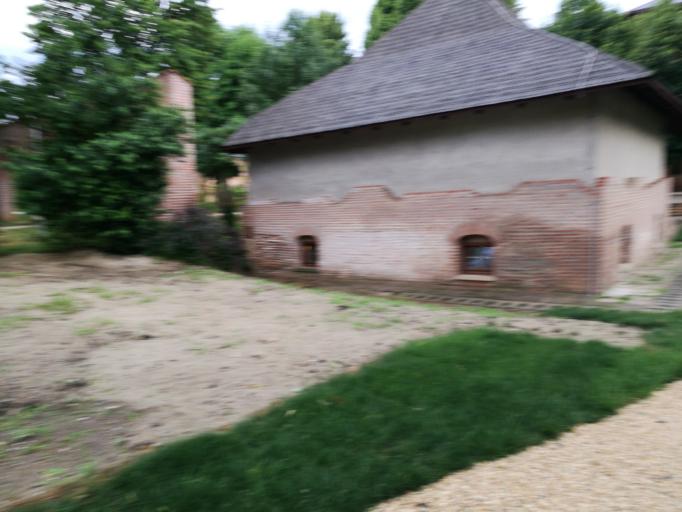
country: RO
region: Ilfov
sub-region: Comuna Mogosoaia
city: Mogosoaia
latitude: 44.5283
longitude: 25.9925
